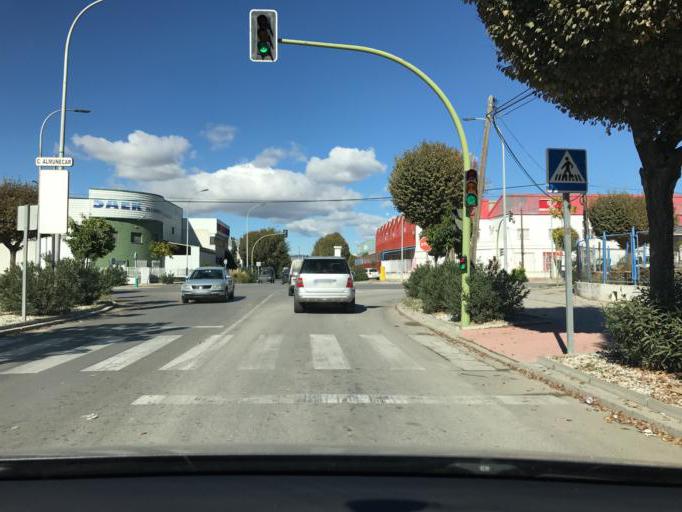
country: ES
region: Andalusia
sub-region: Provincia de Granada
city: Albolote
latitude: 37.2244
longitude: -3.6430
